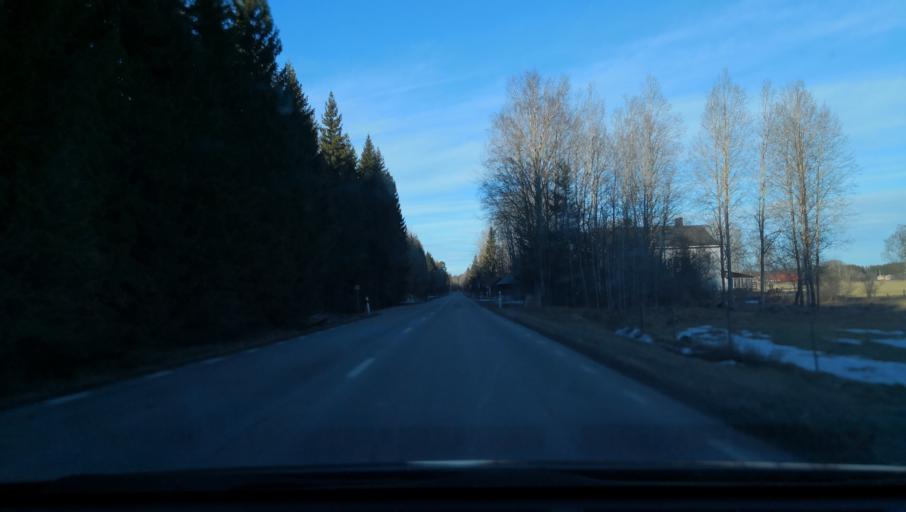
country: SE
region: Uppsala
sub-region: Osthammars Kommun
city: Gimo
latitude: 60.1937
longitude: 18.1908
